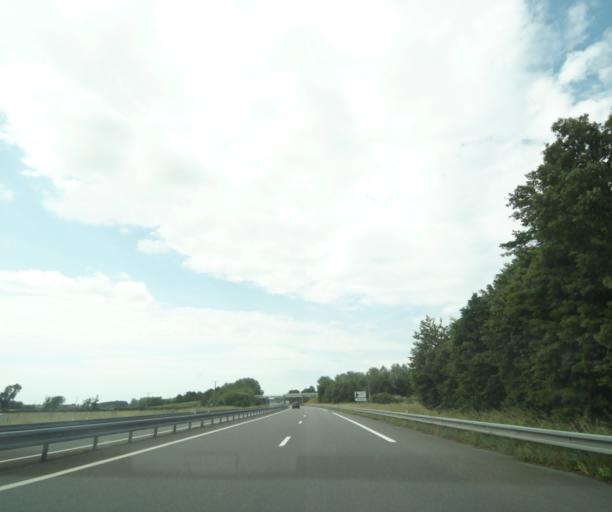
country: FR
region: Pays de la Loire
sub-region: Departement de Maine-et-Loire
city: Brion
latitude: 47.4524
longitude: -0.1778
